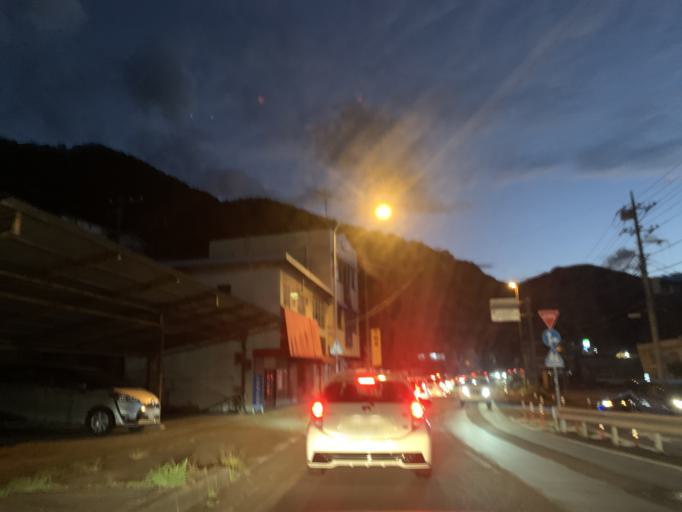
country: JP
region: Yamanashi
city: Otsuki
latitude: 35.6072
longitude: 138.9345
